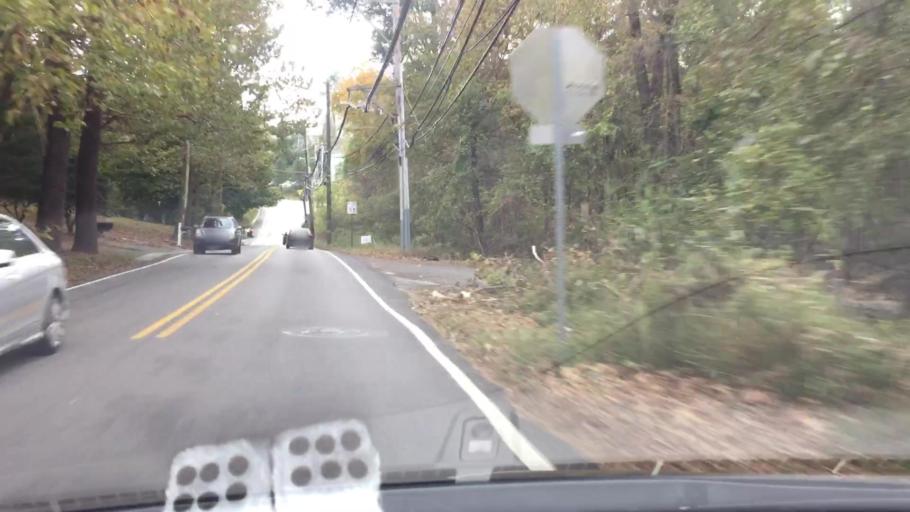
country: US
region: Pennsylvania
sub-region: Delaware County
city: Media
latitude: 39.9185
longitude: -75.4032
